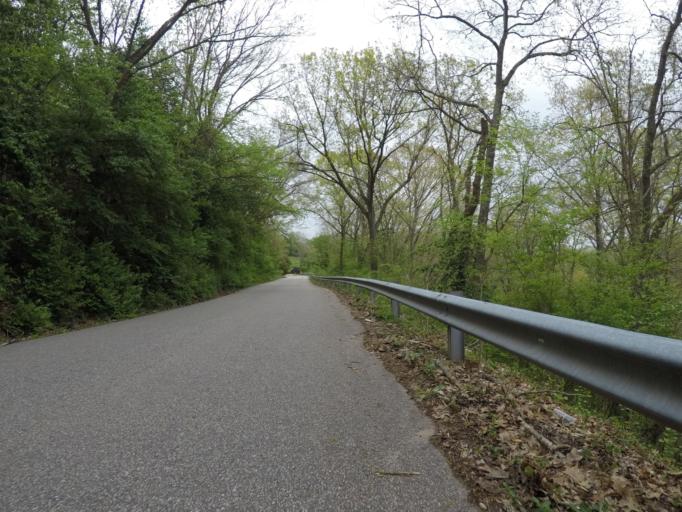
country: US
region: West Virginia
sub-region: Cabell County
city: Barboursville
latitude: 38.4023
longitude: -82.2746
